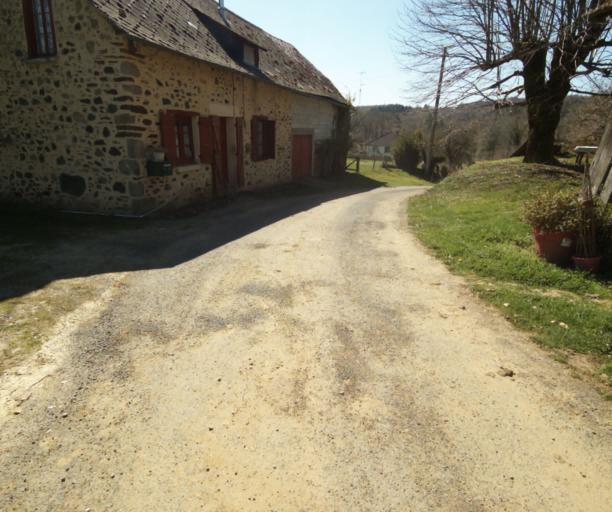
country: FR
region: Limousin
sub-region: Departement de la Correze
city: Saint-Clement
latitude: 45.3216
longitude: 1.6965
